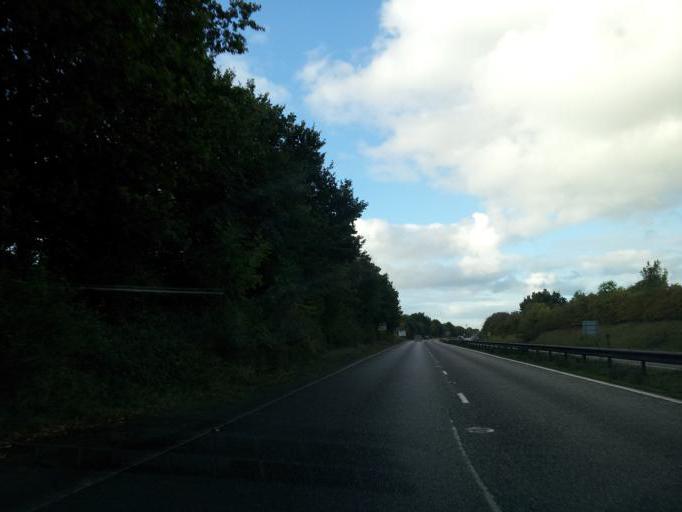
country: GB
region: England
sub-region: Norfolk
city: Brundall
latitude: 52.6367
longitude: 1.4414
